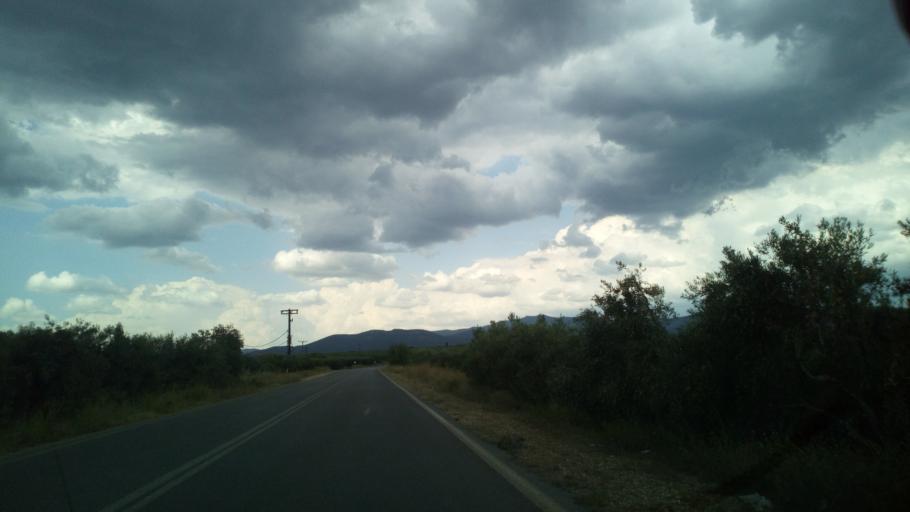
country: GR
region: Central Macedonia
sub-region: Nomos Chalkidikis
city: Kalyves Polygyrou
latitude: 40.2952
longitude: 23.4316
